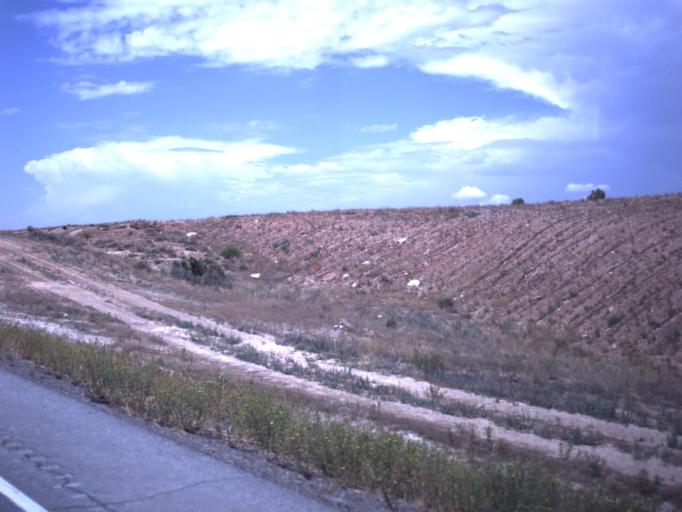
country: US
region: Utah
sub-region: Uintah County
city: Maeser
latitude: 40.3348
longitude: -109.6433
